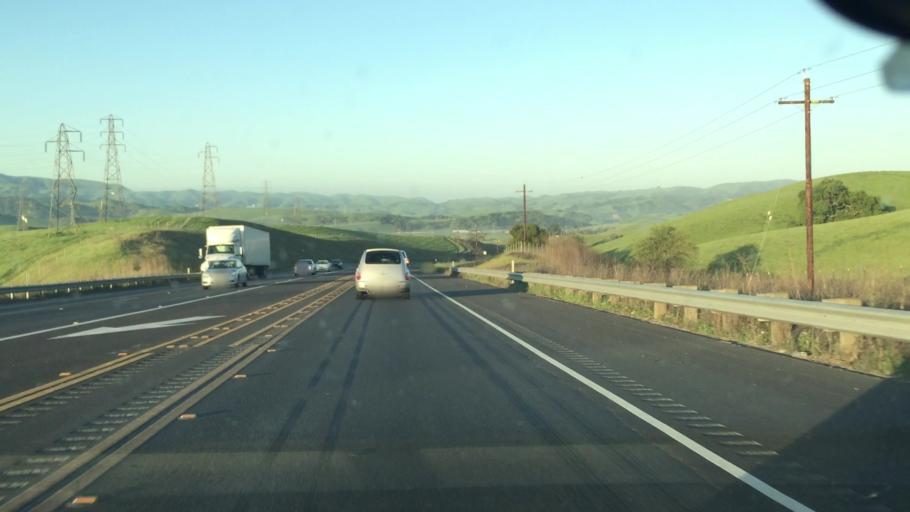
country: US
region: California
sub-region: Alameda County
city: Pleasanton
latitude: 37.6123
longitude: -121.8197
